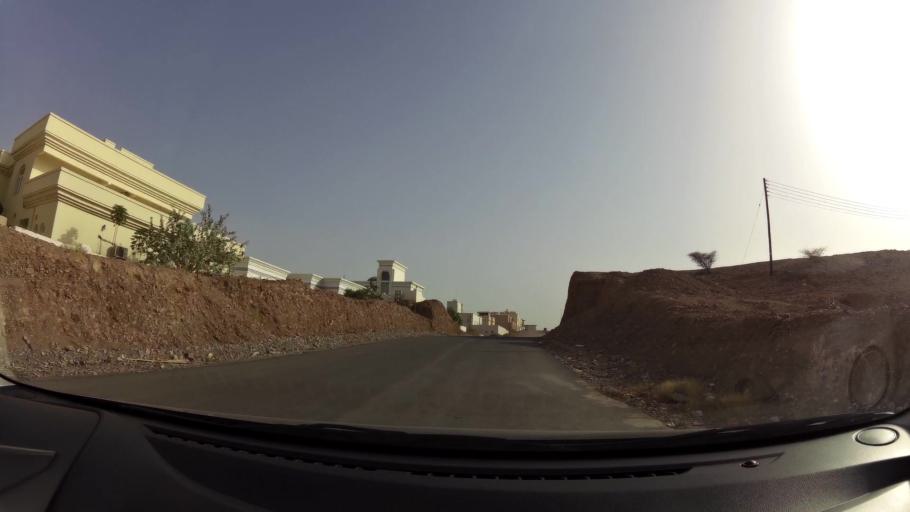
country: OM
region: Muhafazat Masqat
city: Bawshar
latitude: 23.5434
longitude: 58.3646
